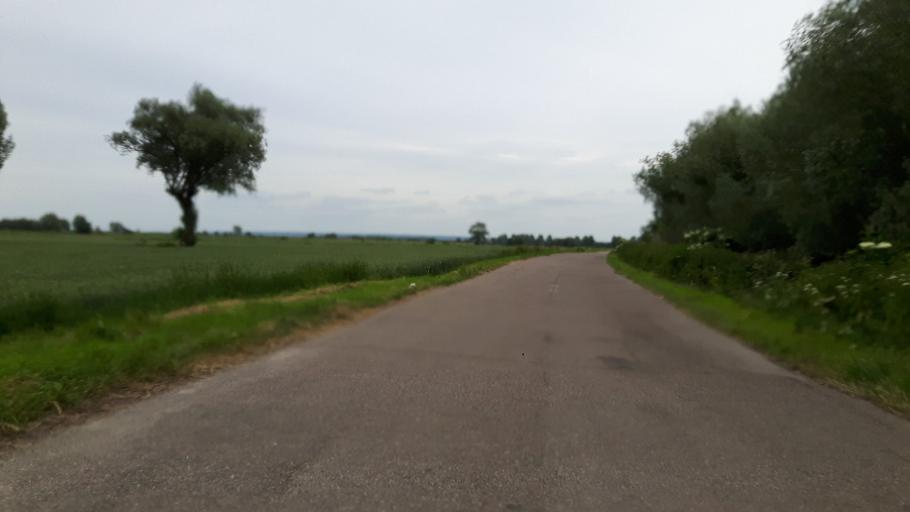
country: PL
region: Pomeranian Voivodeship
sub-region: Powiat nowodworski
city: Sztutowo
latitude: 54.2684
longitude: 19.2186
